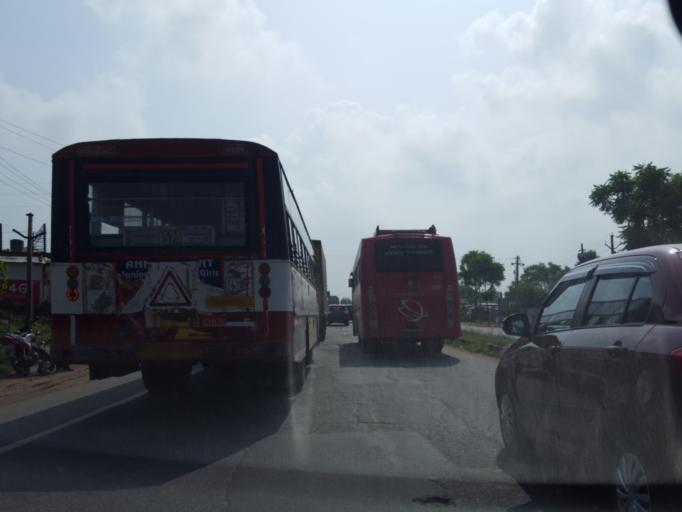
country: IN
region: Telangana
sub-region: Rangareddi
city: Ghatkesar
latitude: 17.3055
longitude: 78.7290
